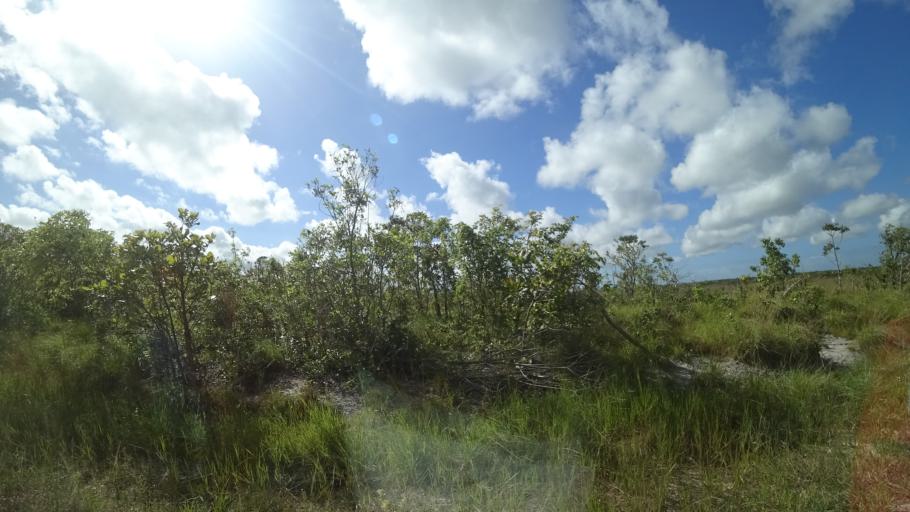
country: MZ
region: Sofala
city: Beira
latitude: -19.6226
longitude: 35.0606
